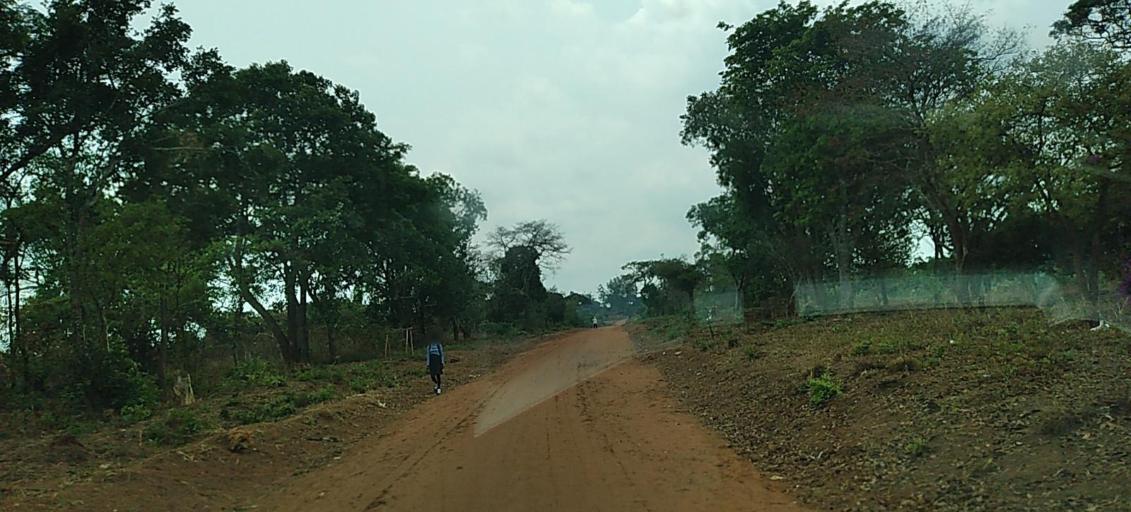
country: ZM
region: North-Western
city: Mwinilunga
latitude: -11.4467
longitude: 24.7490
